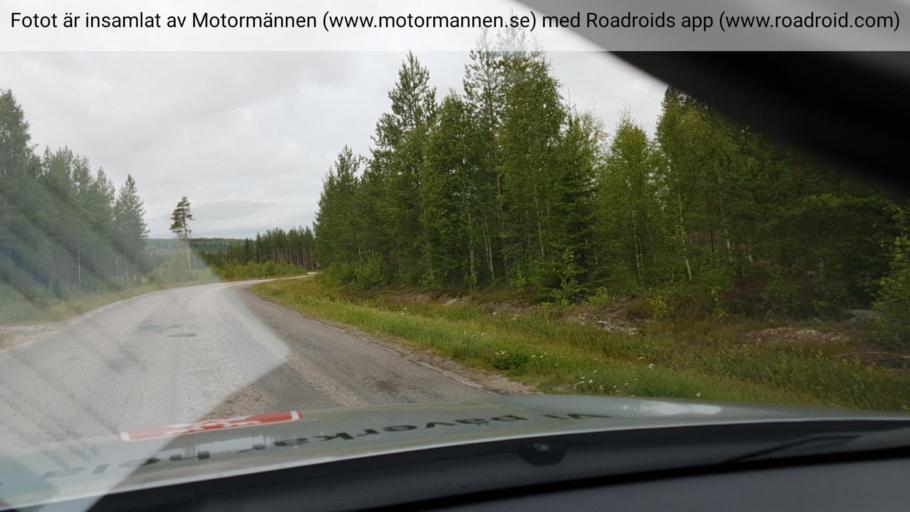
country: SE
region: Norrbotten
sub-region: Bodens Kommun
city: Saevast
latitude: 65.6677
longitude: 21.6840
